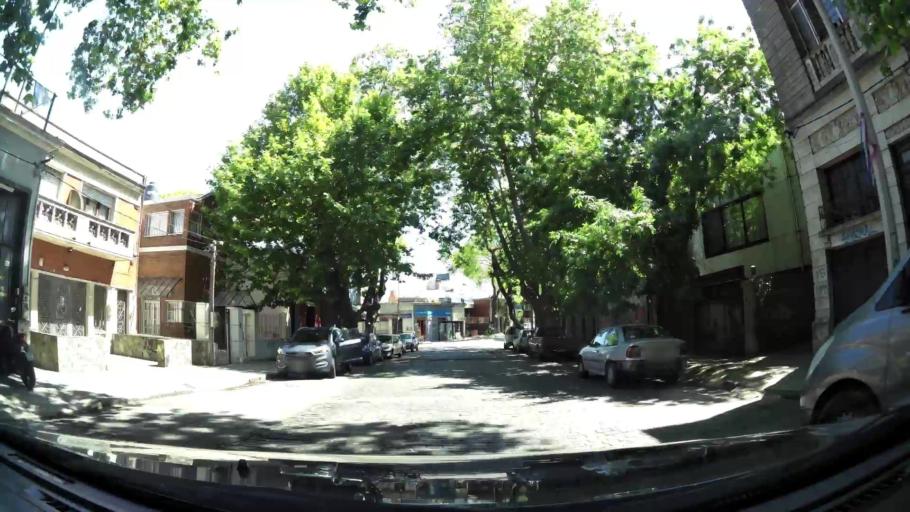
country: UY
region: Montevideo
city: Montevideo
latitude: -34.9181
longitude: -56.1608
